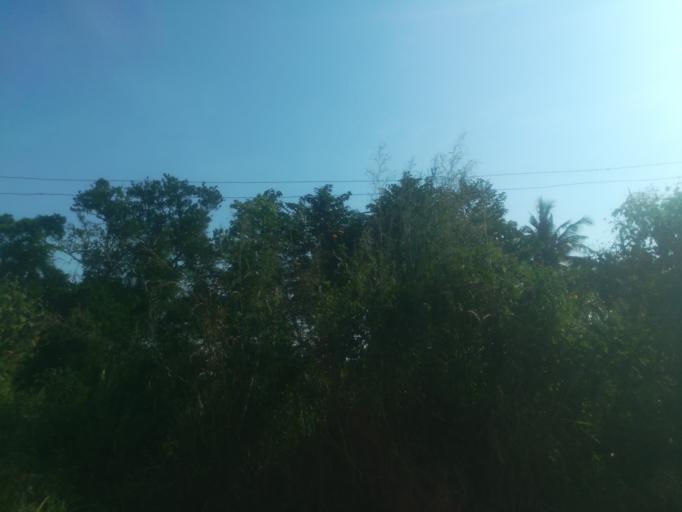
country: NG
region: Ogun
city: Abeokuta
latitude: 7.1401
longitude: 3.2515
